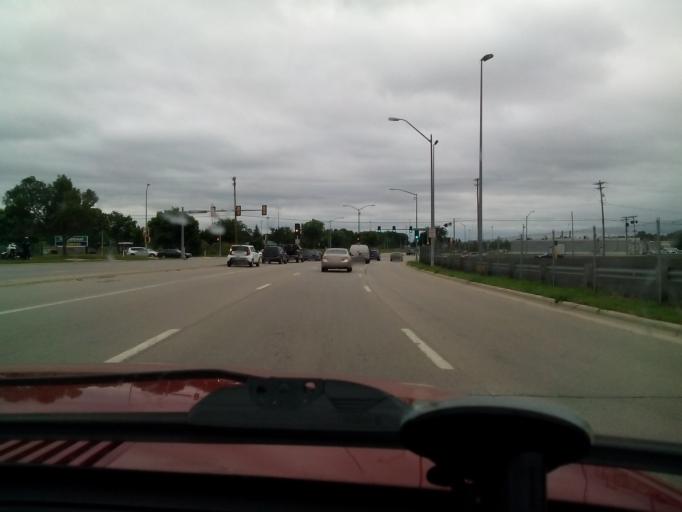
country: US
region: Wisconsin
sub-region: Dane County
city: Maple Bluff
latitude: 43.1077
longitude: -89.3545
